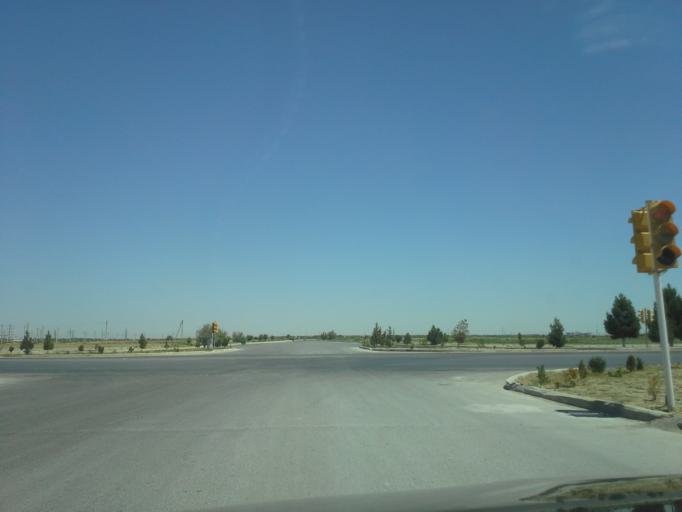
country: TM
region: Ahal
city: Ashgabat
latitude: 38.0019
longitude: 58.3161
